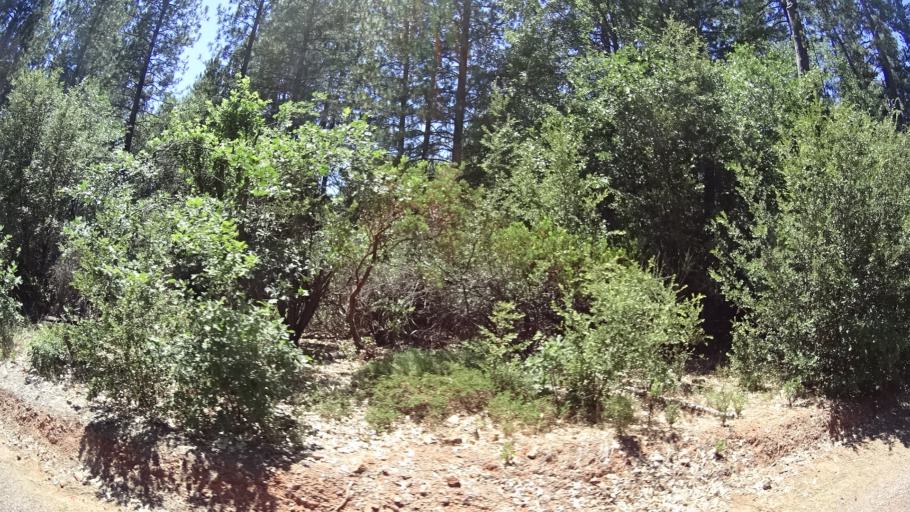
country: US
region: California
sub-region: Calaveras County
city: Mountain Ranch
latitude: 38.3312
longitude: -120.5185
